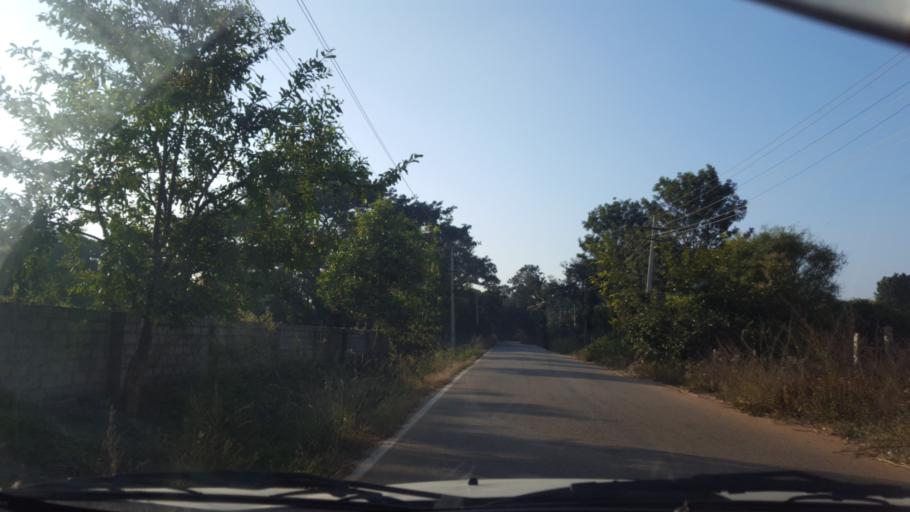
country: IN
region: Karnataka
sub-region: Bangalore Urban
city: Yelahanka
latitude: 13.1728
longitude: 77.5973
